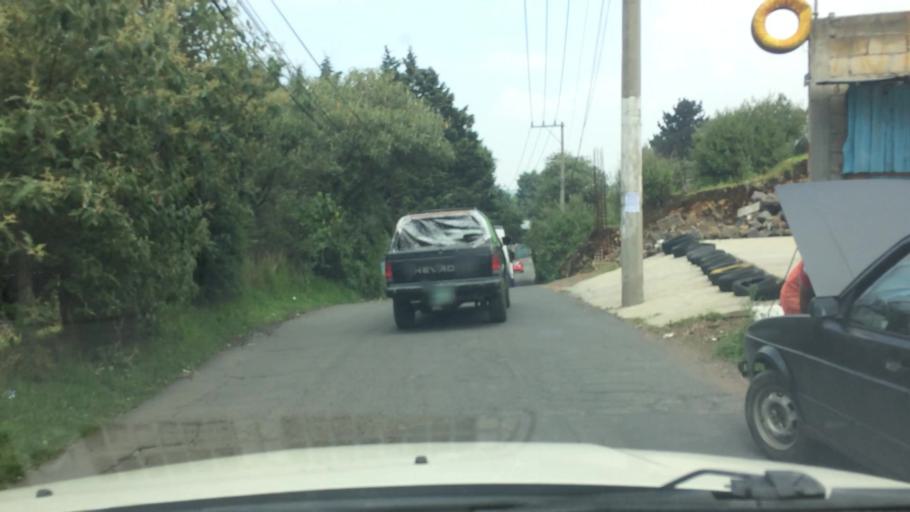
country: MX
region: Mexico City
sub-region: Tlalpan
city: Lomas de Tepemecatl
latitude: 19.2253
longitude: -99.2110
